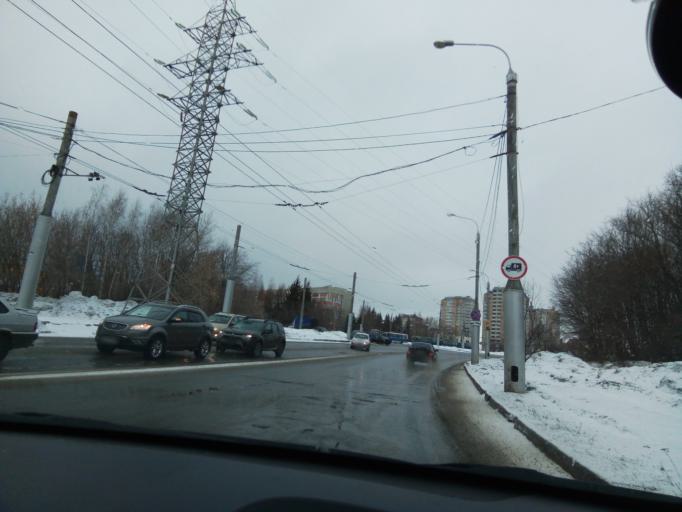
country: RU
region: Chuvashia
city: Novyye Lapsary
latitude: 56.1318
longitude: 47.1676
